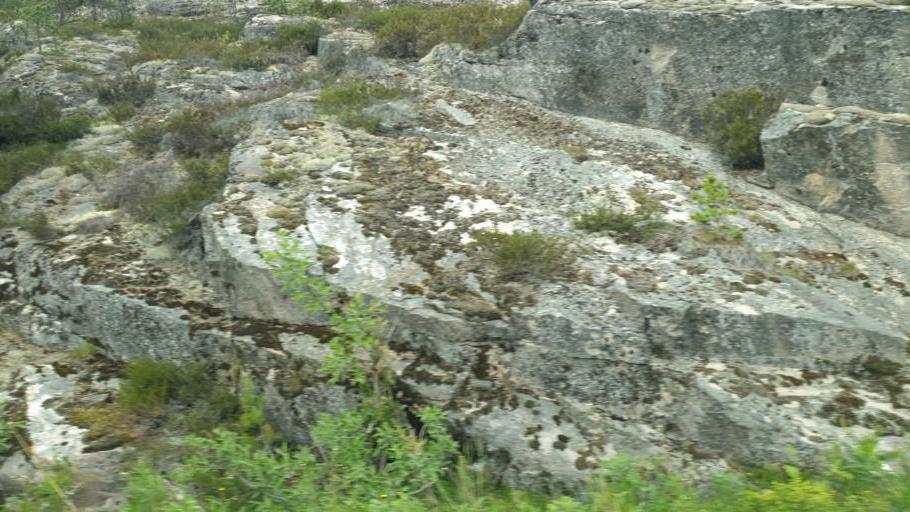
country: NO
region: Sor-Trondelag
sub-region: Trondheim
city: Trondheim
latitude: 63.5665
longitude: 10.3390
